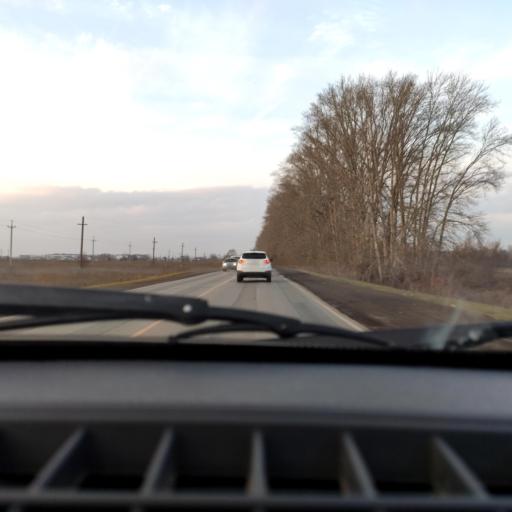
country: RU
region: Bashkortostan
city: Avdon
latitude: 54.7278
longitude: 55.8058
